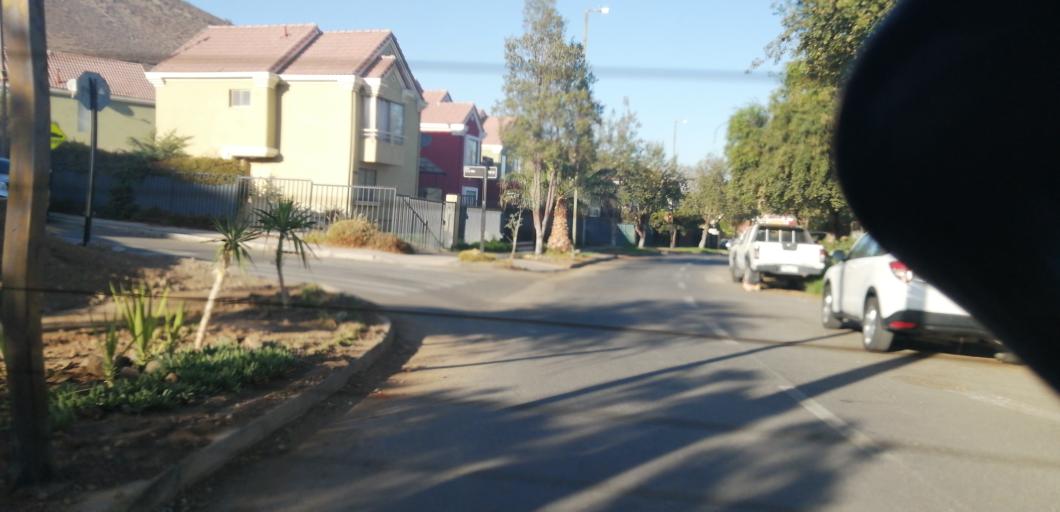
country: CL
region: Santiago Metropolitan
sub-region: Provincia de Santiago
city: Lo Prado
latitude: -33.4475
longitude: -70.8383
